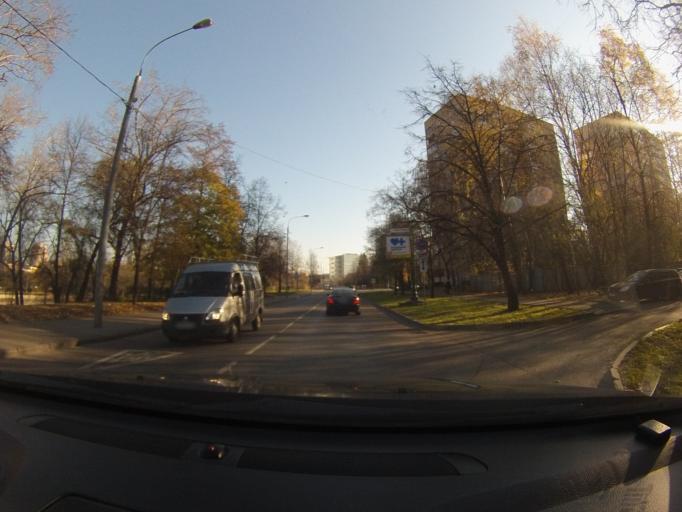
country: RU
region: Moskovskaya
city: Levoberezhnyy
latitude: 55.8504
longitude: 37.4872
